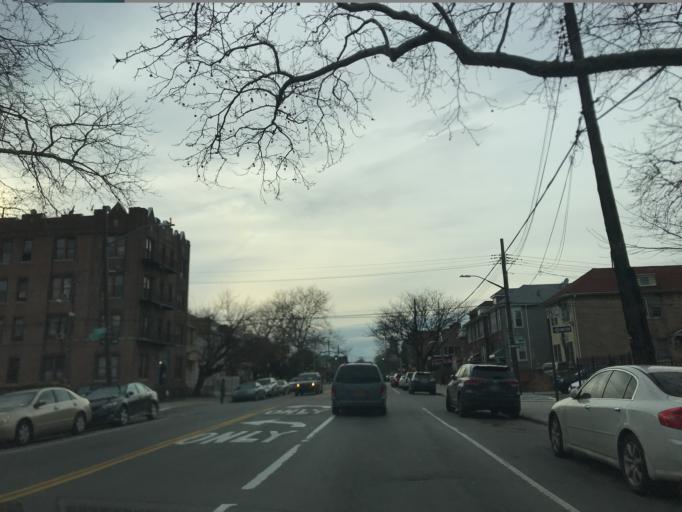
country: US
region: New York
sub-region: Kings County
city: Brooklyn
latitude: 40.6534
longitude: -73.9377
